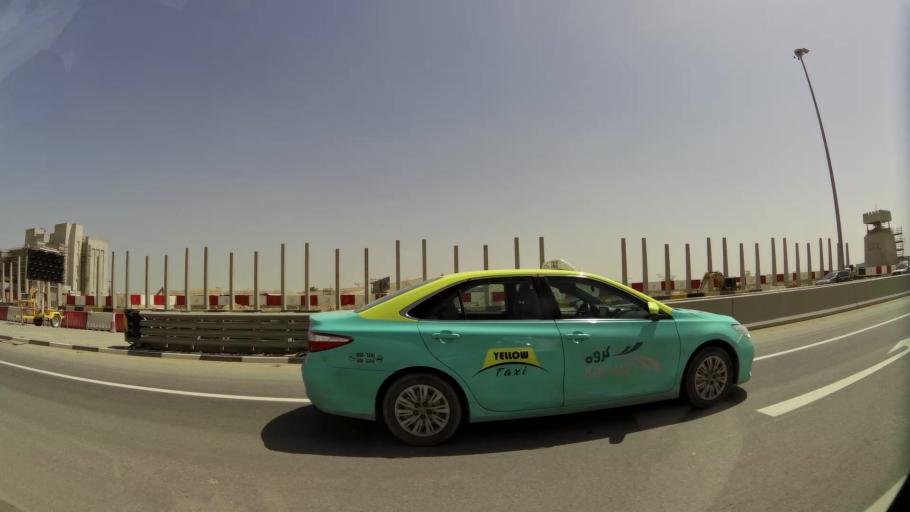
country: QA
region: Baladiyat Umm Salal
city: Umm Salal Muhammad
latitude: 25.3677
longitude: 51.4531
